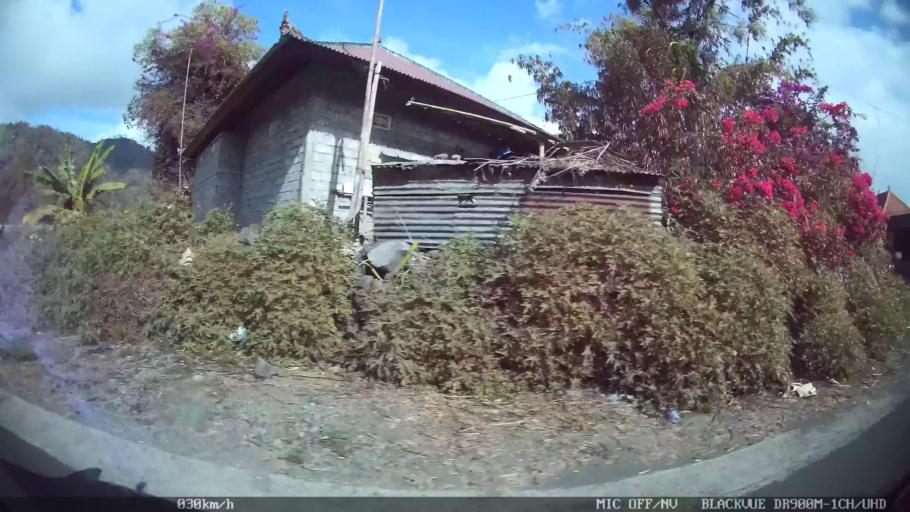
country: ID
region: Bali
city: Banjar Trunyan
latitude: -8.2265
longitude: 115.4109
